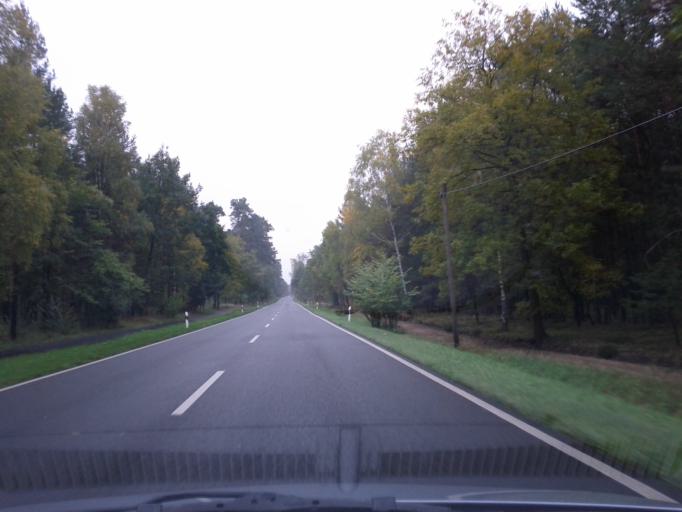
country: DE
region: Brandenburg
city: Grunheide
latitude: 52.3998
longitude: 13.8250
